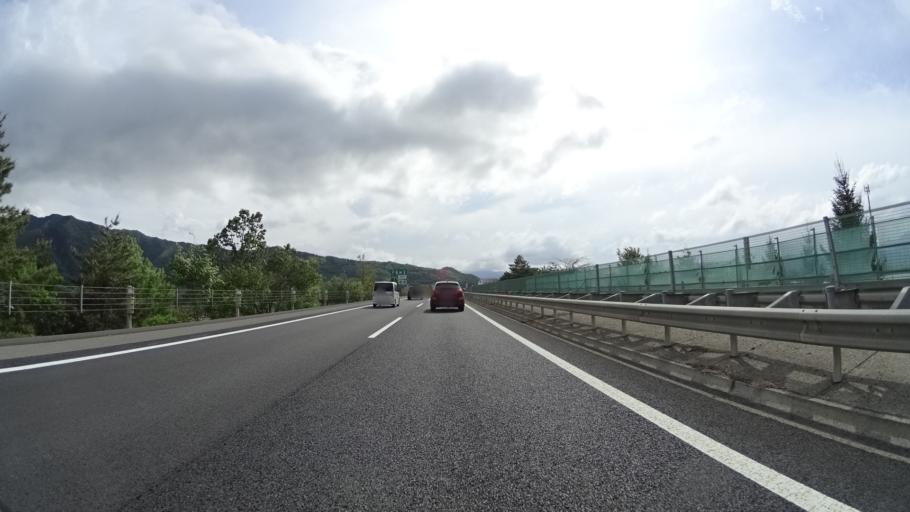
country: JP
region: Nagano
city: Nagano-shi
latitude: 36.5703
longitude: 138.1943
